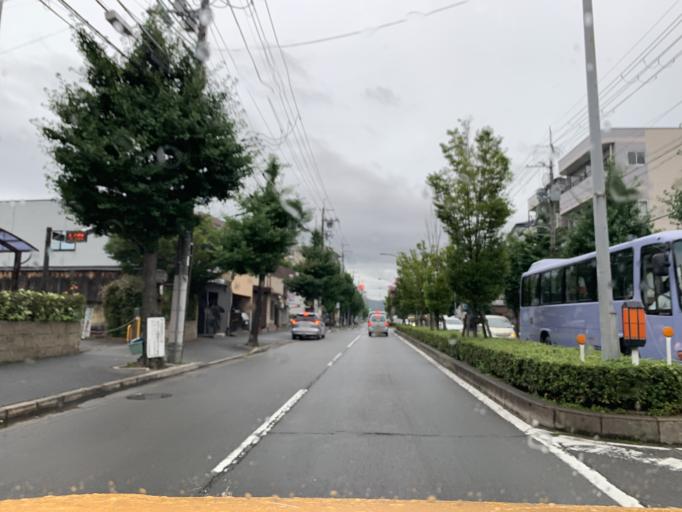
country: JP
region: Kyoto
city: Kyoto
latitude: 35.0109
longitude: 135.7234
